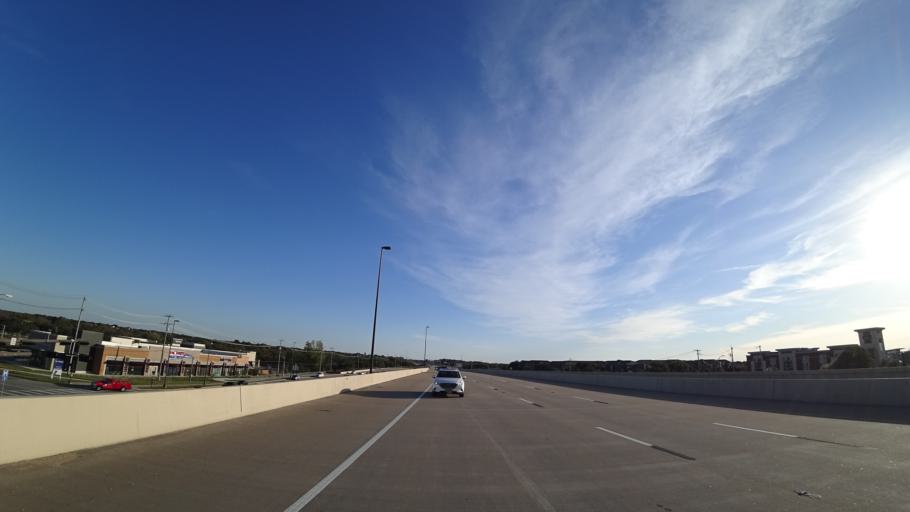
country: US
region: Texas
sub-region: Williamson County
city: Cedar Park
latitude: 30.5254
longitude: -97.8161
